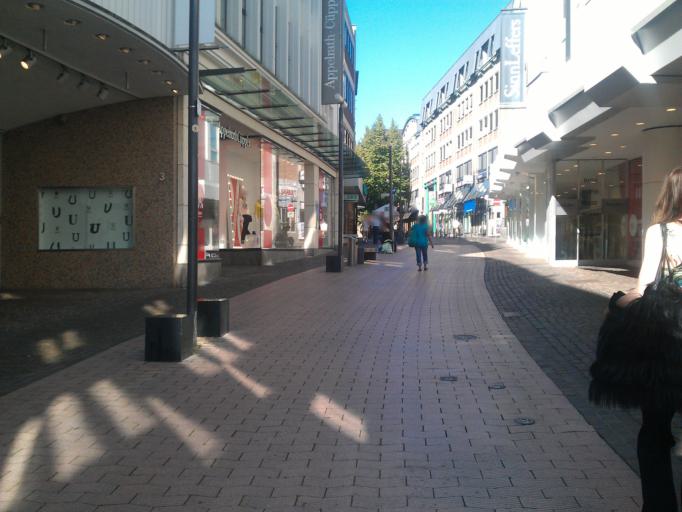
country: DE
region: North Rhine-Westphalia
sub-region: Regierungsbezirk Koln
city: Aachen
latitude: 50.7772
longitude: 6.0854
